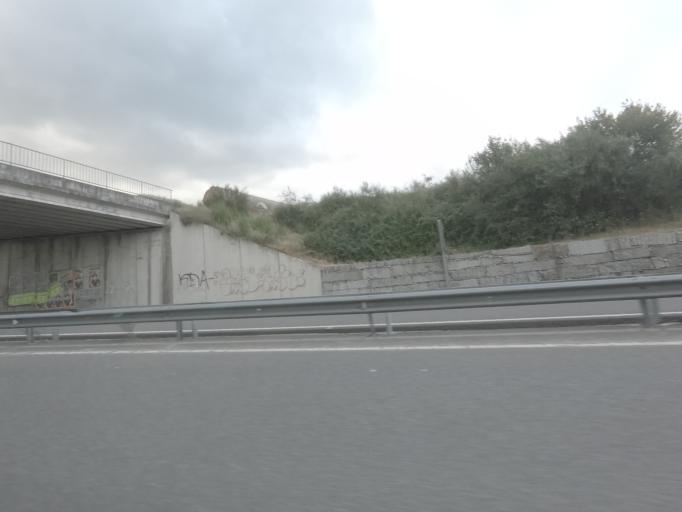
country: ES
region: Galicia
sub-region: Provincia de Ourense
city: Taboadela
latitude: 42.2871
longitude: -7.8281
